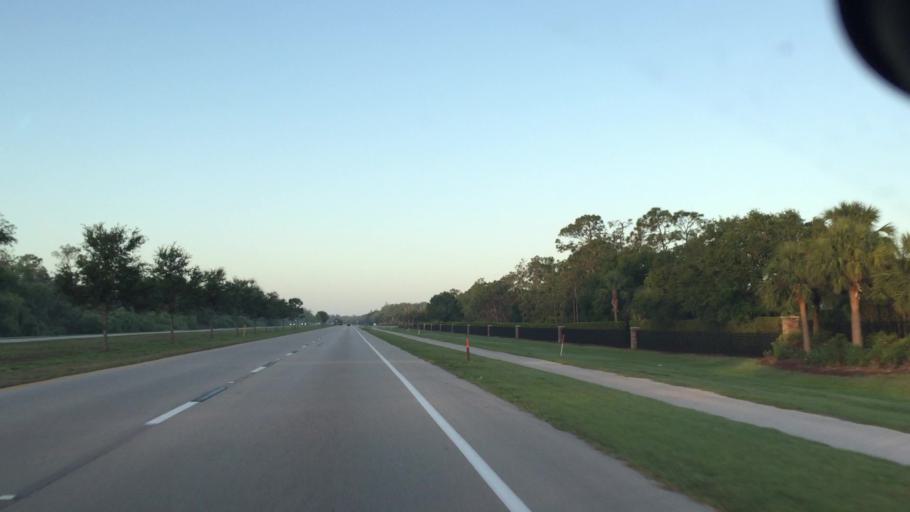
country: US
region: Florida
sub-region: Lee County
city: Fort Myers
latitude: 26.5909
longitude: -81.8155
